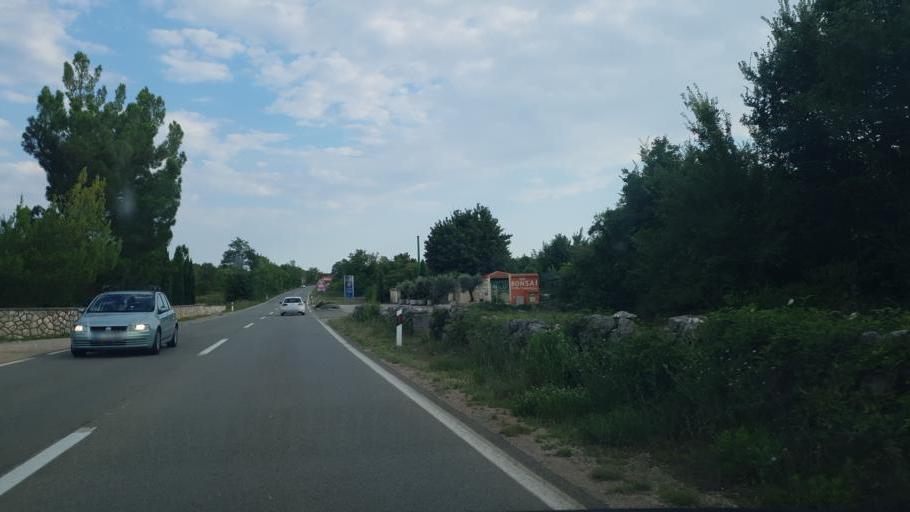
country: HR
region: Primorsko-Goranska
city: Njivice
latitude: 45.1485
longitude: 14.5472
